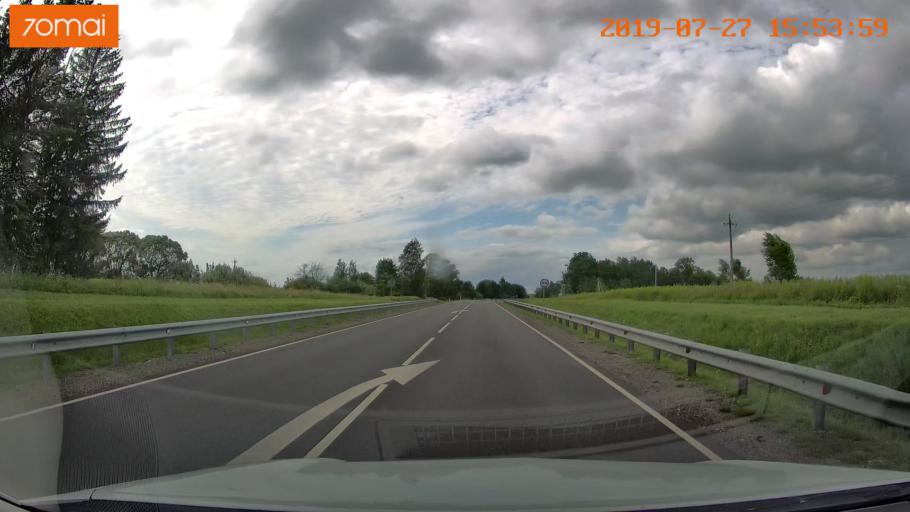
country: RU
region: Kaliningrad
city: Chernyakhovsk
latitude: 54.6053
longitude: 21.9456
